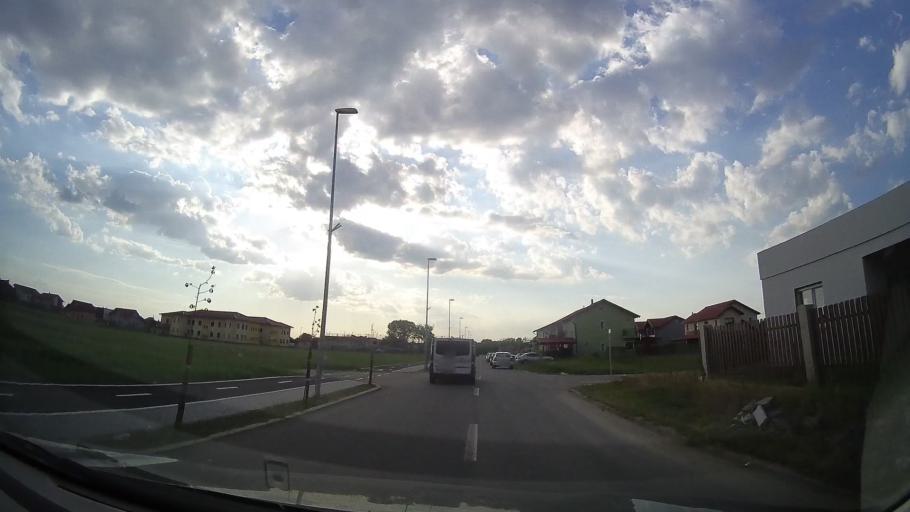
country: RO
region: Timis
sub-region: Comuna Dumbravita
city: Dumbravita
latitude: 45.7992
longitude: 21.2523
